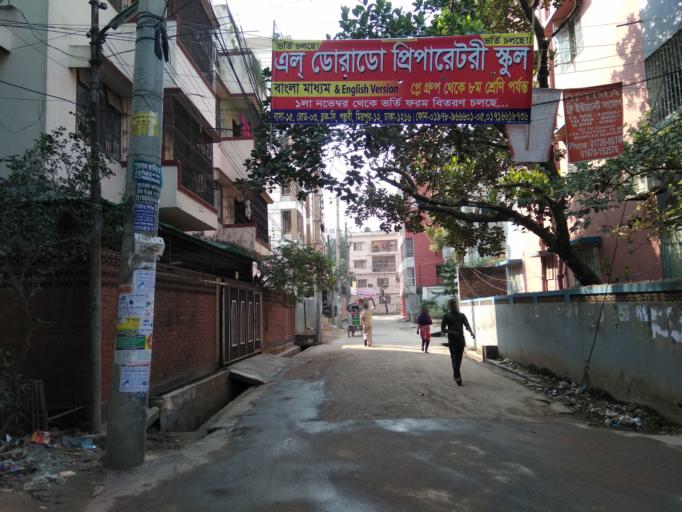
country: BD
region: Dhaka
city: Tungi
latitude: 23.8277
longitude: 90.3616
